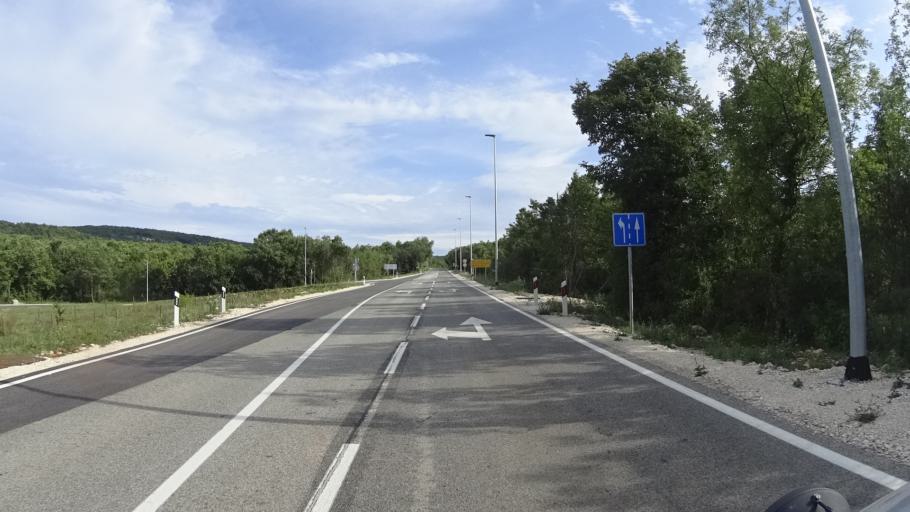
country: HR
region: Istarska
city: Rasa
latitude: 45.0632
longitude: 14.0898
